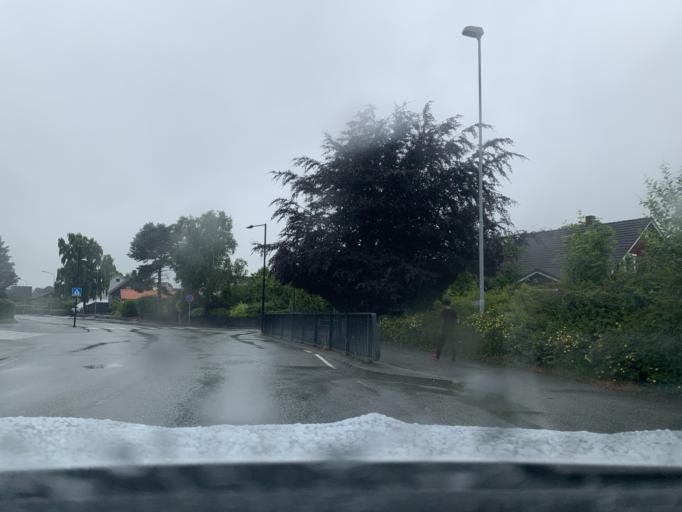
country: NO
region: Rogaland
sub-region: Time
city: Bryne
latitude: 58.7313
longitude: 5.6471
